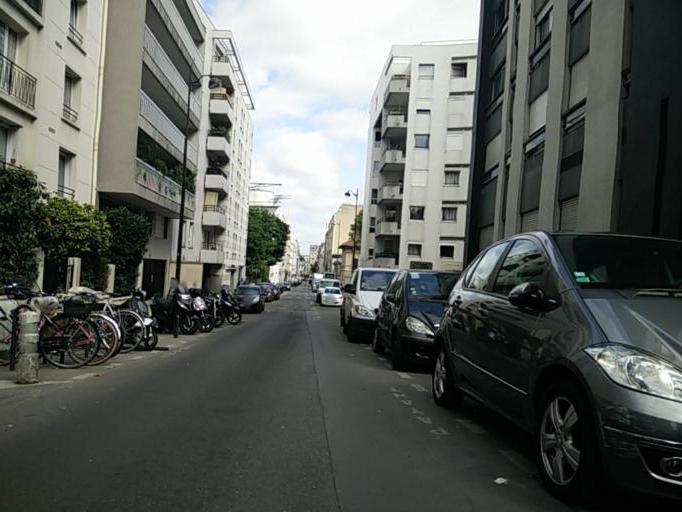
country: FR
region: Ile-de-France
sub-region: Departement de Seine-Saint-Denis
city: Le Pre-Saint-Gervais
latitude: 48.8835
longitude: 2.3878
